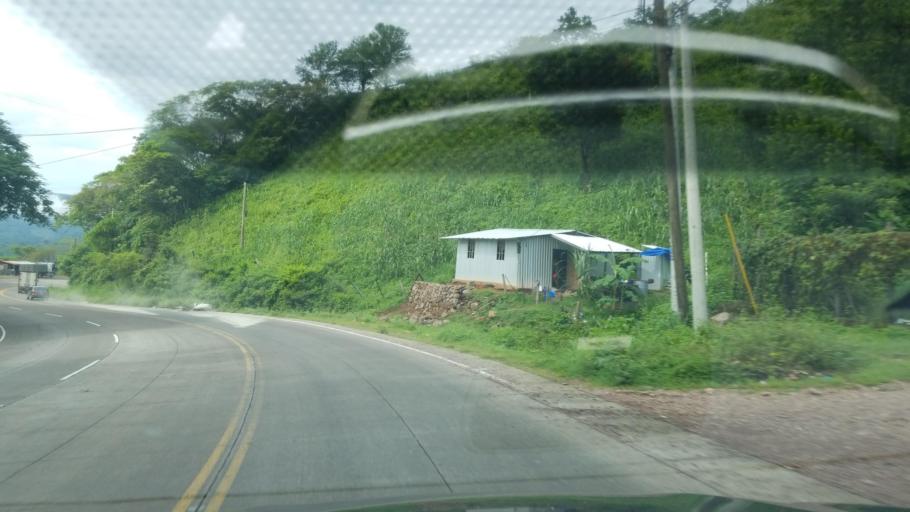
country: HN
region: Francisco Morazan
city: El Porvenir
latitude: 13.7020
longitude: -87.3162
